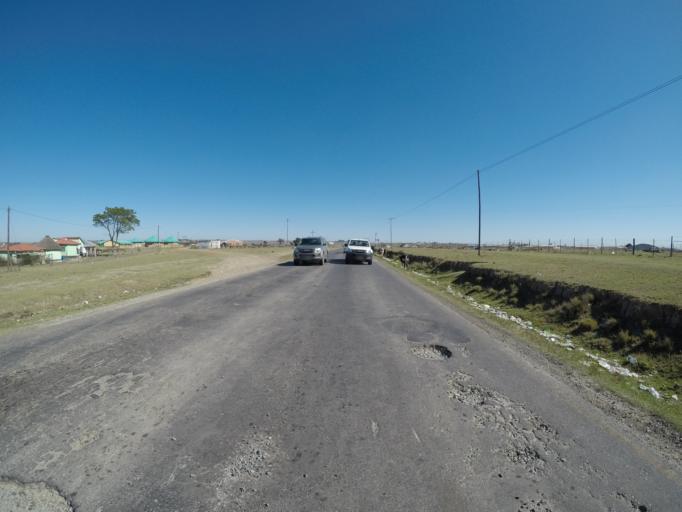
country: ZA
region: Eastern Cape
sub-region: OR Tambo District Municipality
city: Mthatha
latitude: -31.7875
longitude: 28.7430
